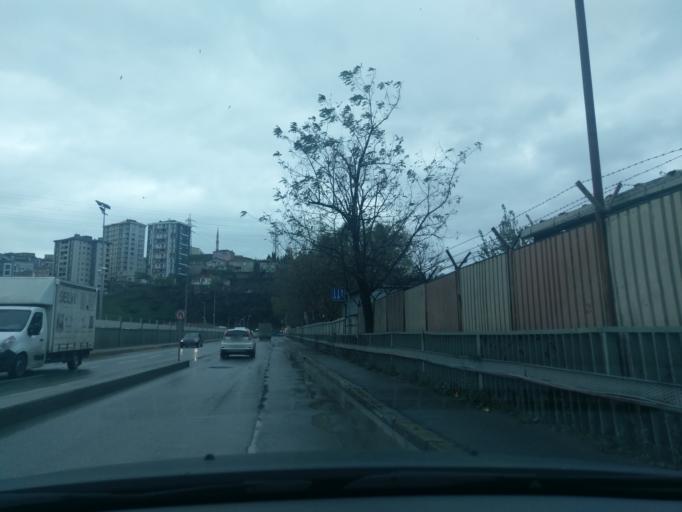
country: TR
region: Istanbul
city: Sisli
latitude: 41.0836
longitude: 28.9516
